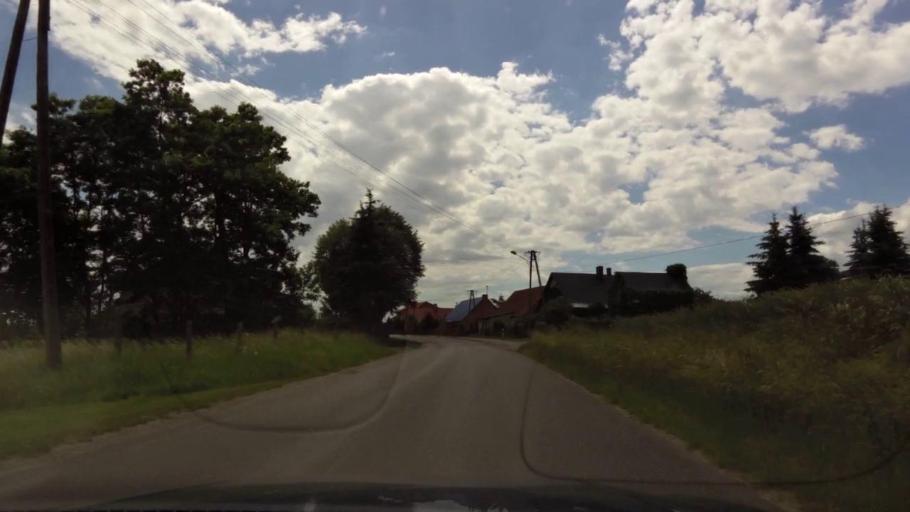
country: PL
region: West Pomeranian Voivodeship
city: Trzcinsko Zdroj
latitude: 52.9840
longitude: 14.7176
